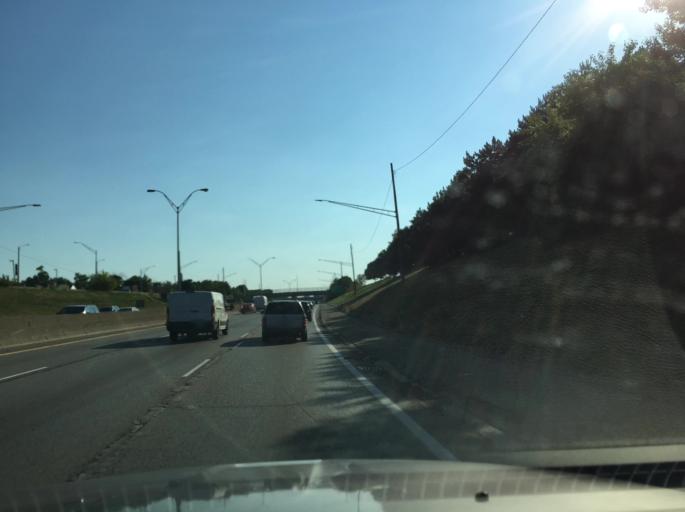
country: US
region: Michigan
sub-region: Wayne County
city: Hamtramck
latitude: 42.3786
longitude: -83.0352
